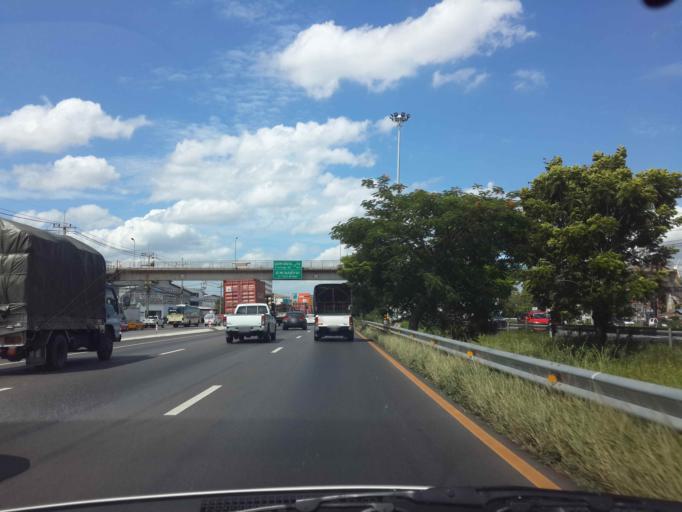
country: TH
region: Bangkok
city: Bang Bon
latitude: 13.5967
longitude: 100.3643
